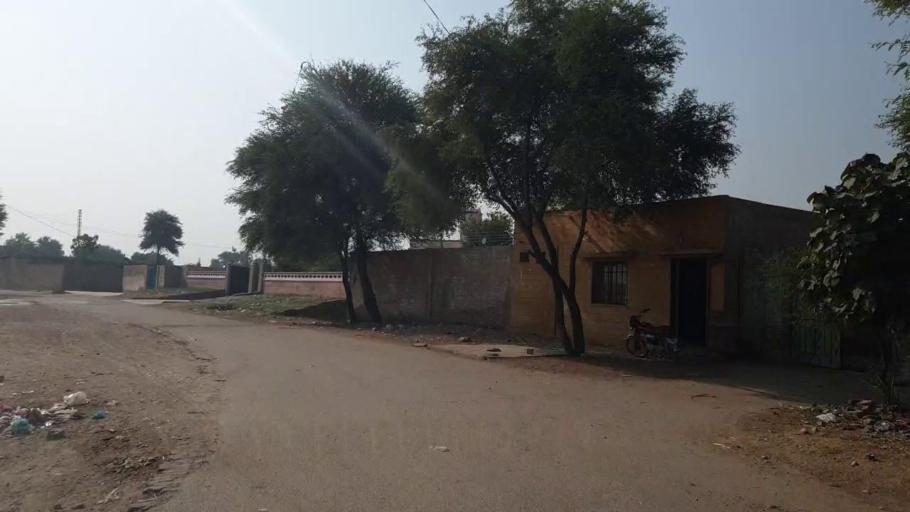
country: PK
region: Sindh
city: Kotri
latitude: 25.3569
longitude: 68.3080
